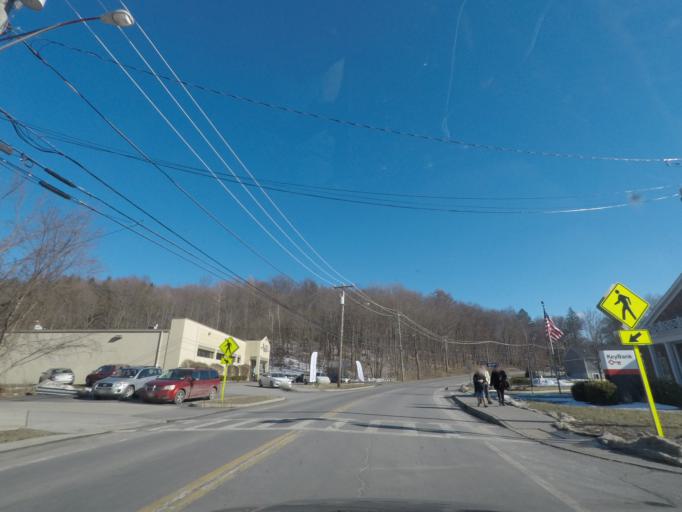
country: US
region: New York
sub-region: Columbia County
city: Chatham
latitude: 42.3565
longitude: -73.5999
